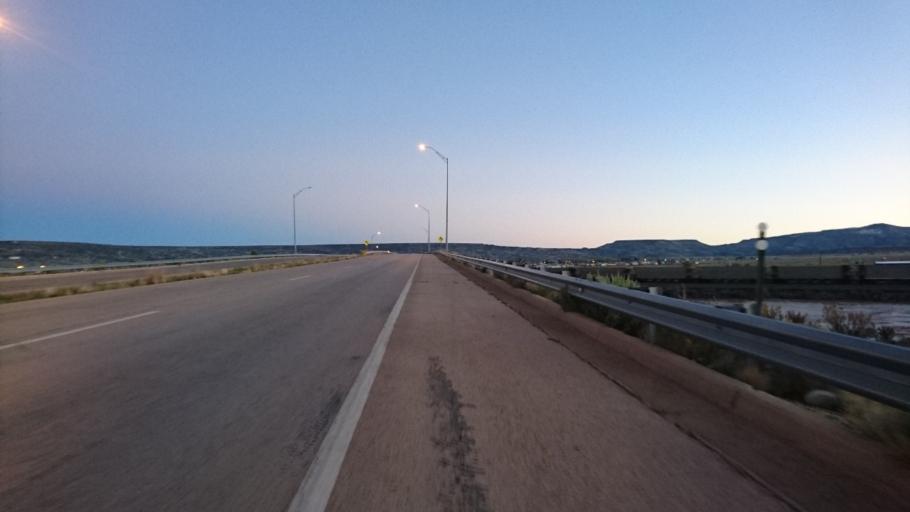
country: US
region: New Mexico
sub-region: Cibola County
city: Grants
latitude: 35.1353
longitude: -107.8276
